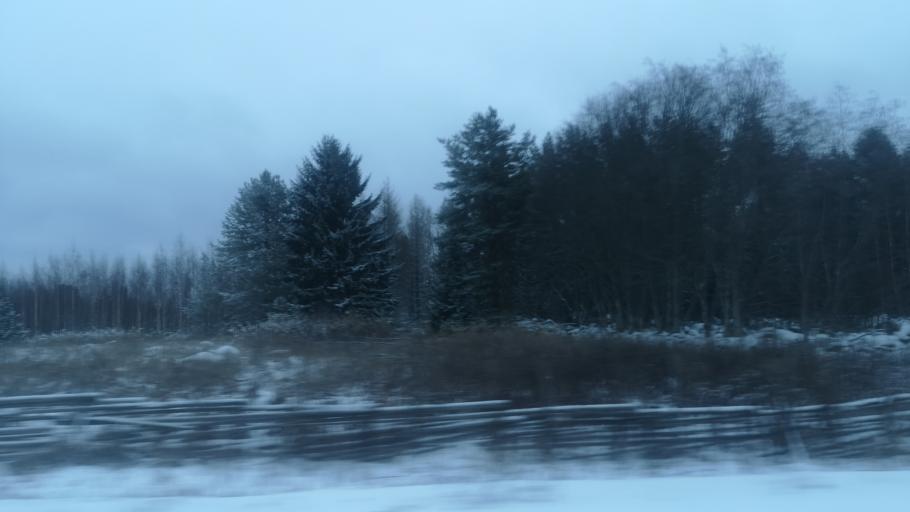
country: FI
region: Southern Savonia
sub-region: Savonlinna
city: Enonkoski
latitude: 62.0426
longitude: 28.7062
